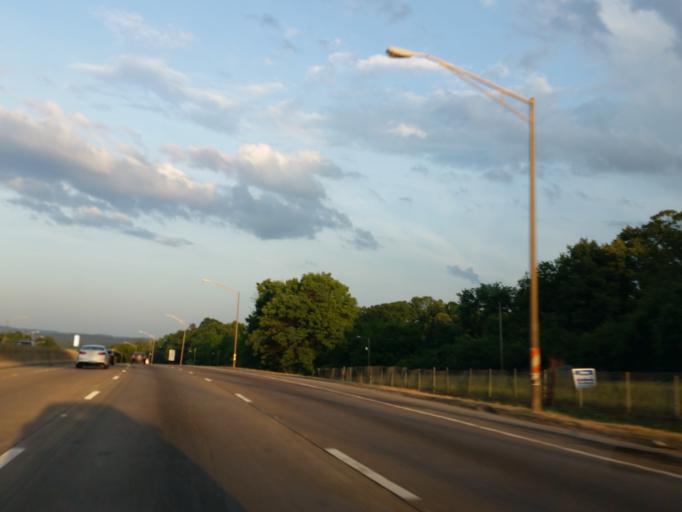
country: US
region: Tennessee
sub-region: Hamilton County
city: East Ridge
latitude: 35.0135
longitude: -85.2505
